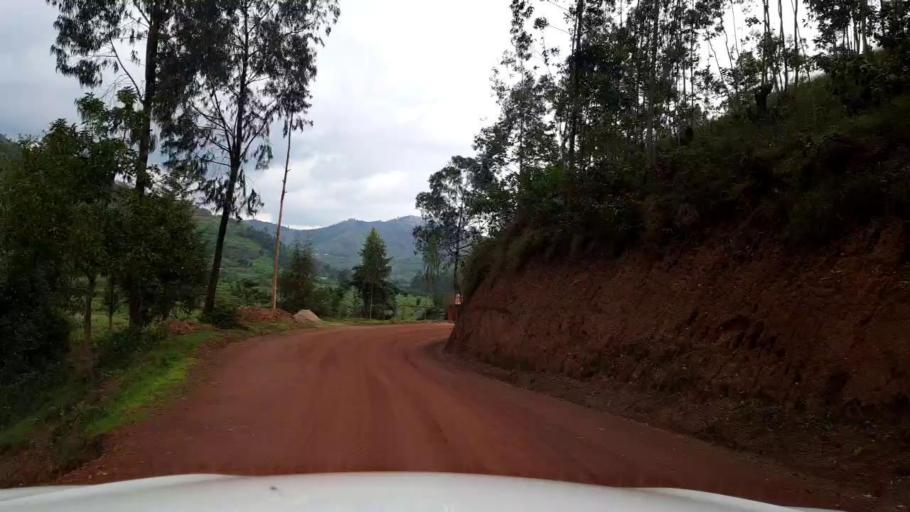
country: RW
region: Northern Province
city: Musanze
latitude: -1.6724
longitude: 29.7994
